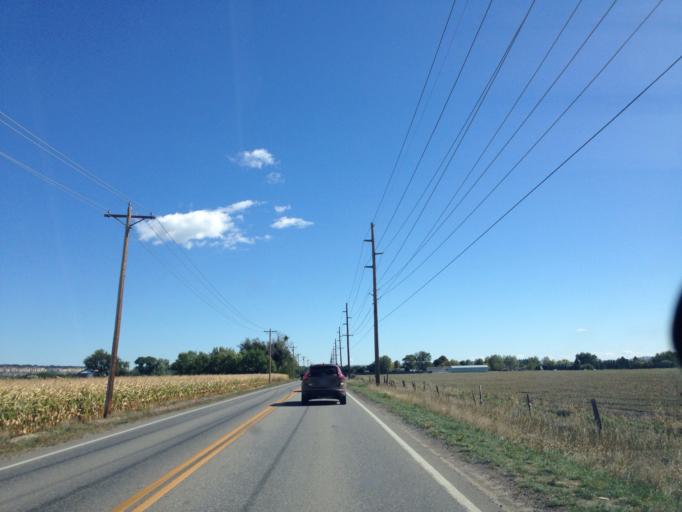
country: US
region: Montana
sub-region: Yellowstone County
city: Billings
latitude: 45.7841
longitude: -108.6464
